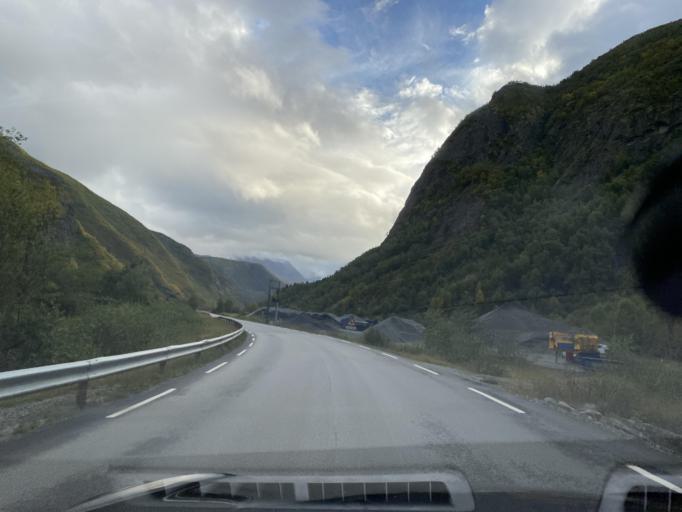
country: NO
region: Oppland
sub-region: Lom
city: Fossbergom
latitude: 61.7810
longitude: 8.4308
